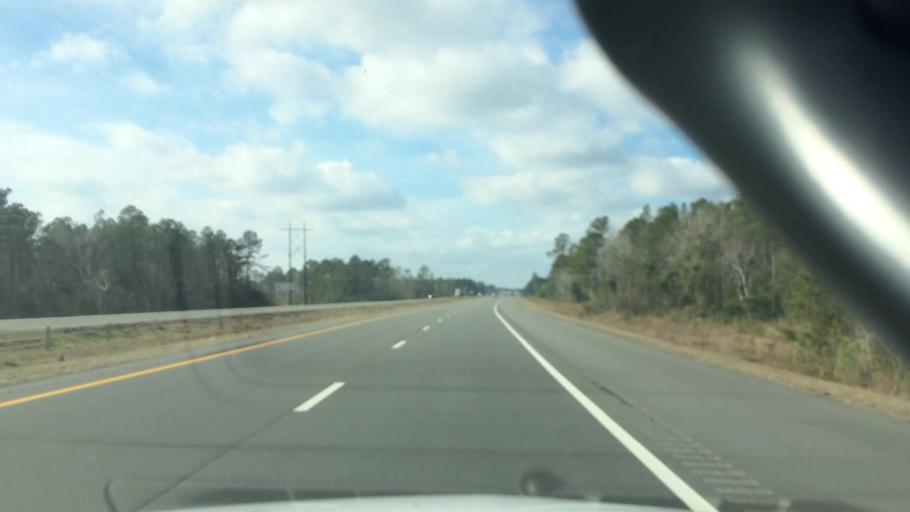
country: US
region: North Carolina
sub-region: Brunswick County
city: Leland
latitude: 34.2740
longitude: -78.0335
